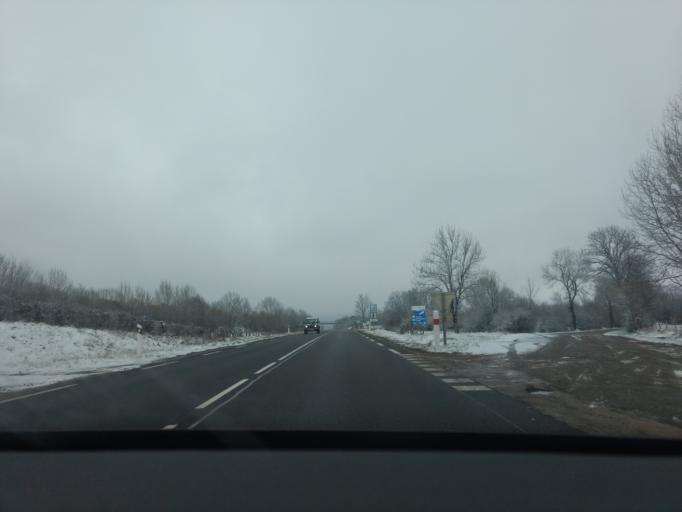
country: FR
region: Franche-Comte
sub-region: Departement du Jura
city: Champagnole
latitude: 46.7727
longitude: 5.9053
